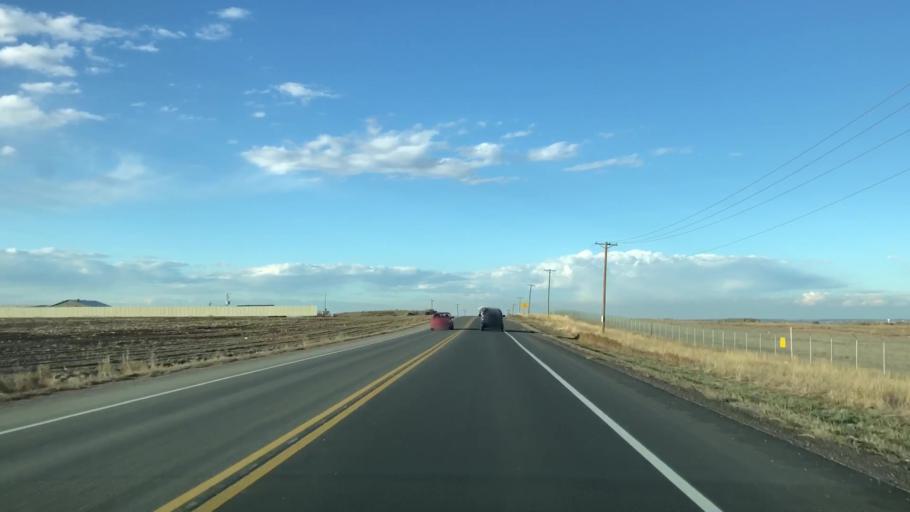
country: US
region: Colorado
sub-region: Larimer County
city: Loveland
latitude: 40.4566
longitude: -105.0204
